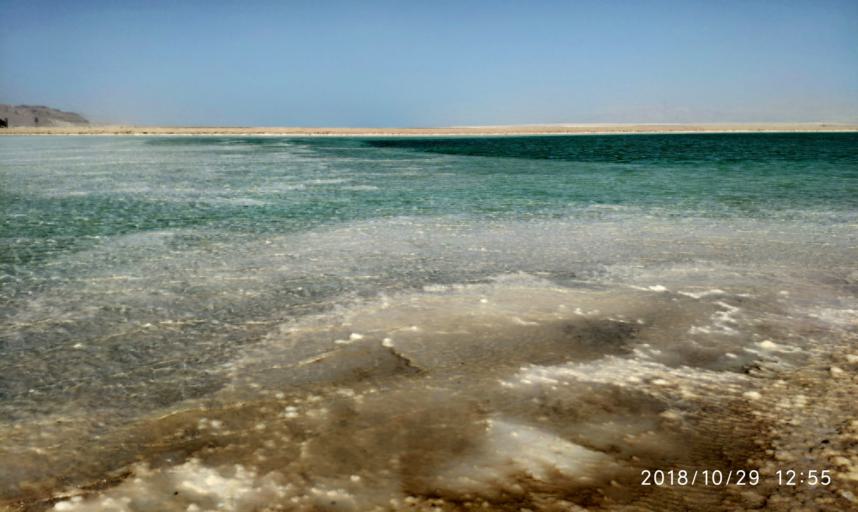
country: IL
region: Southern District
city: `En Boqeq
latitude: 31.1750
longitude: 35.3692
